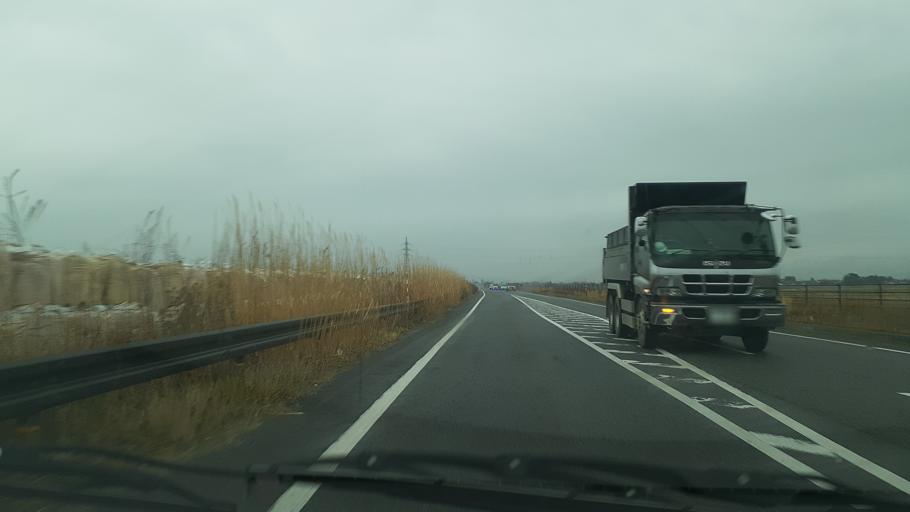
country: JP
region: Niigata
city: Kameda-honcho
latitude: 37.8692
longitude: 139.1458
